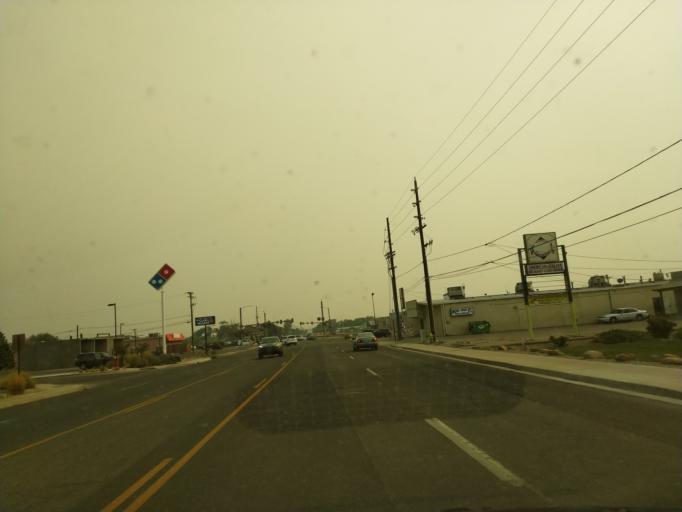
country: US
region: Colorado
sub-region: Mesa County
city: Fruitvale
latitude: 39.0796
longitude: -108.4966
